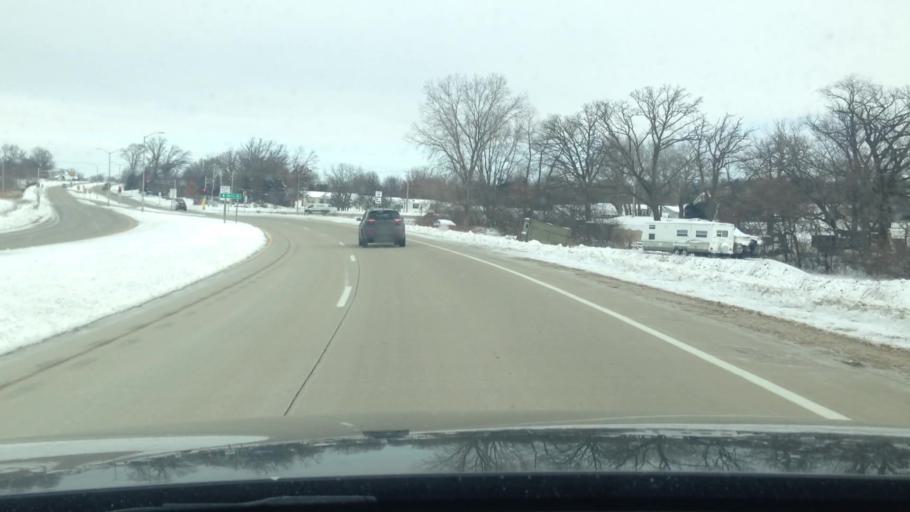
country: US
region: Wisconsin
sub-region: Walworth County
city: Lake Geneva
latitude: 42.5628
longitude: -88.4142
